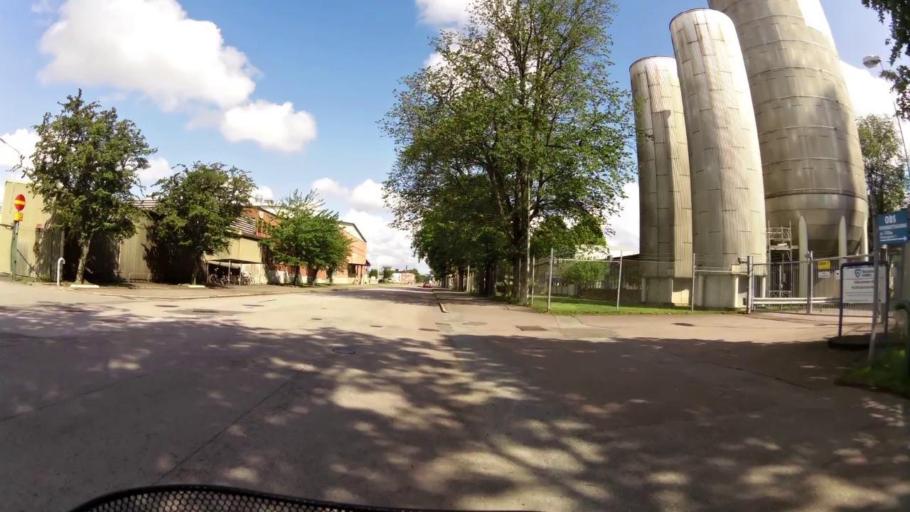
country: SE
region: OEstergoetland
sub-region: Linkopings Kommun
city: Linkoping
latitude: 58.4191
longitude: 15.6233
